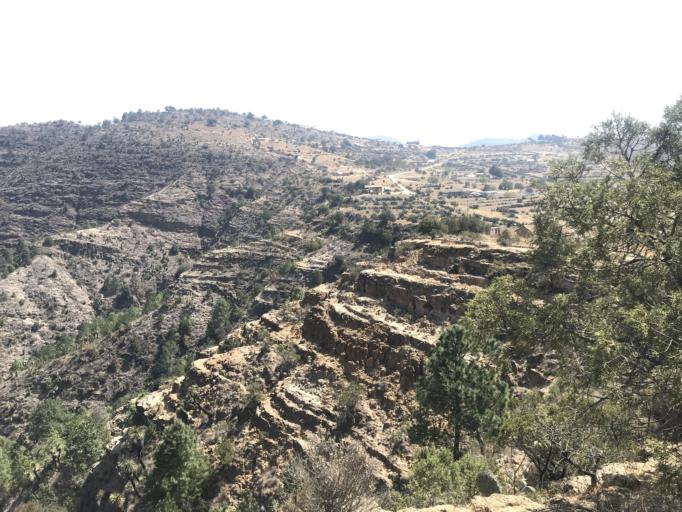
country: MX
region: Puebla
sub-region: Zautla
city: San Andres Yahuitlalpan
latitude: 19.6772
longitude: -97.8110
